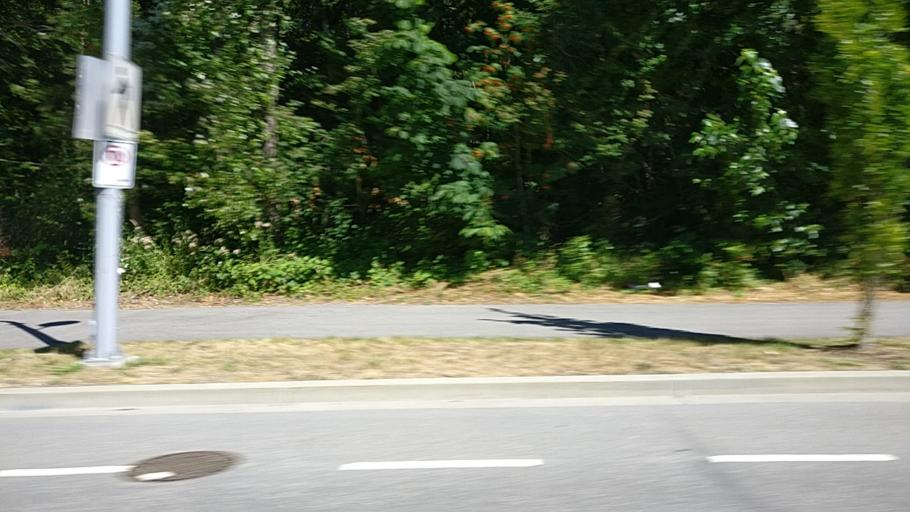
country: CA
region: British Columbia
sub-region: Greater Vancouver Regional District
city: White Rock
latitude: 49.0385
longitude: -122.8295
